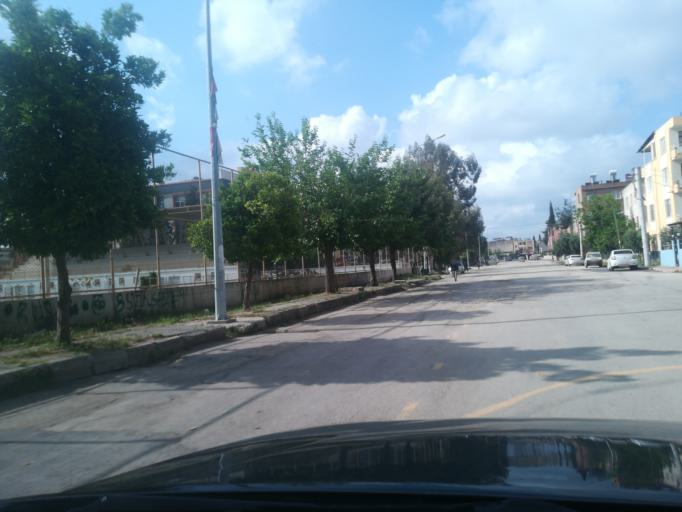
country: TR
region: Adana
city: Adana
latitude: 37.0097
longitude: 35.3501
